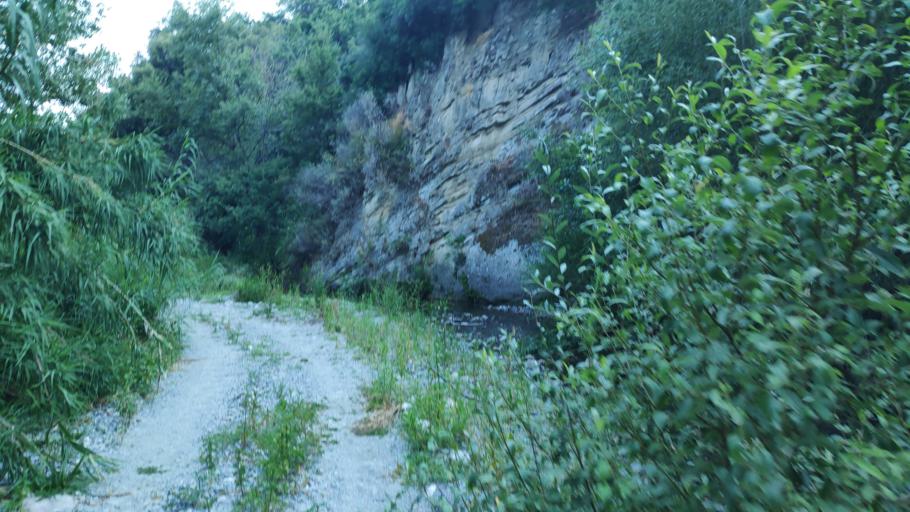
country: IT
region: Calabria
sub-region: Provincia di Reggio Calabria
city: Placanica
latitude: 38.4162
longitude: 16.4367
